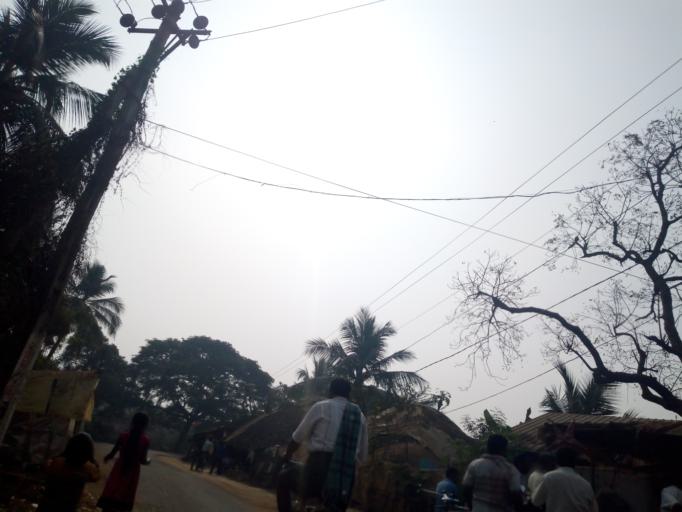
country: IN
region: Andhra Pradesh
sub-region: West Godavari
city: Tadepallegudem
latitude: 16.8121
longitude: 81.3640
